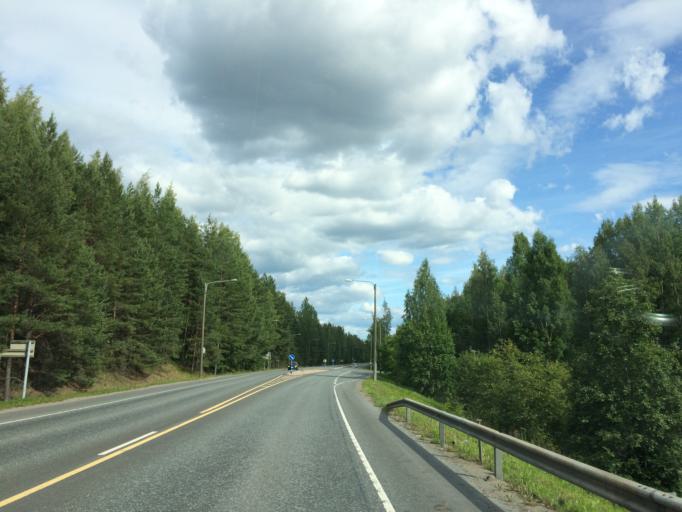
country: FI
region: Haeme
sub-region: Haemeenlinna
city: Haemeenlinna
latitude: 60.9806
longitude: 24.5246
